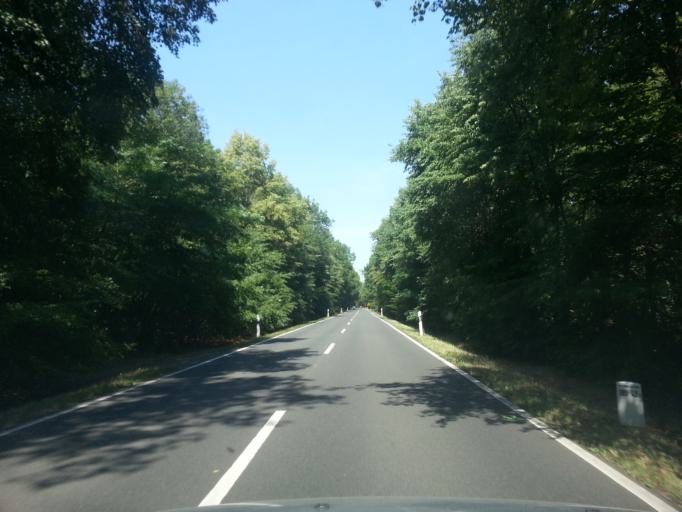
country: DE
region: Hesse
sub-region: Regierungsbezirk Darmstadt
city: Gross-Rohrheim
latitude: 49.7007
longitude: 8.5162
